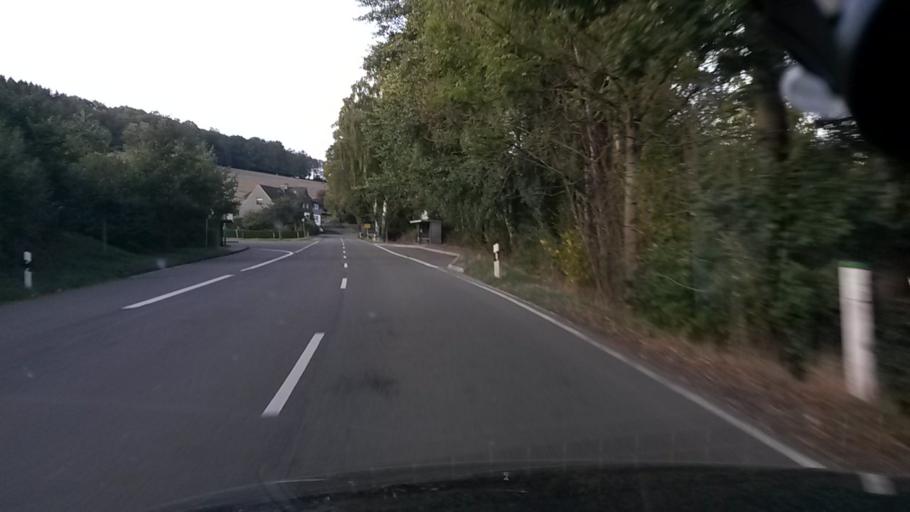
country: DE
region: North Rhine-Westphalia
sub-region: Regierungsbezirk Koln
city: Marienheide
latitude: 51.0674
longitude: 7.5151
